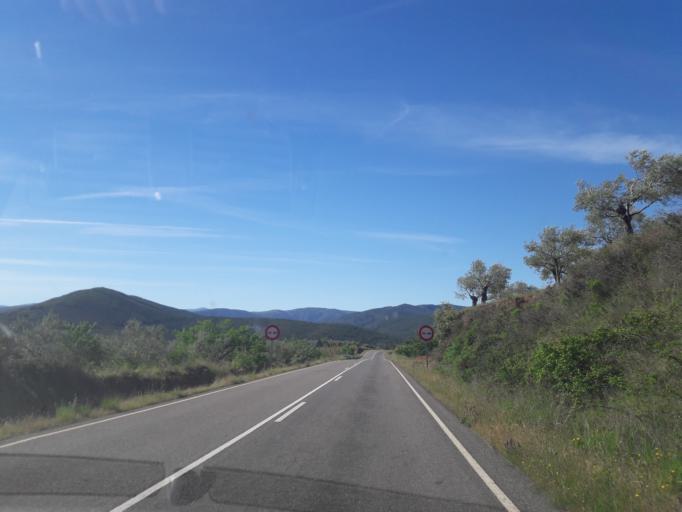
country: ES
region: Castille and Leon
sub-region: Provincia de Salamanca
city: Sotoserrano
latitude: 40.4280
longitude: -6.0330
